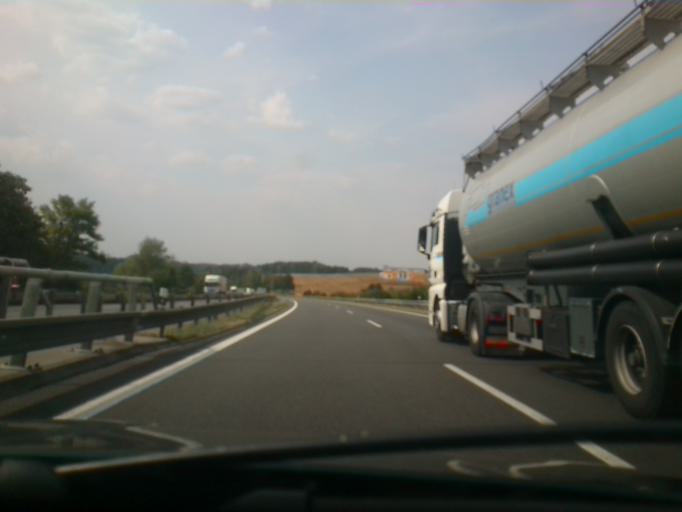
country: CZ
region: Central Bohemia
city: Trhovy Stepanov
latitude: 49.7390
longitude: 15.0395
